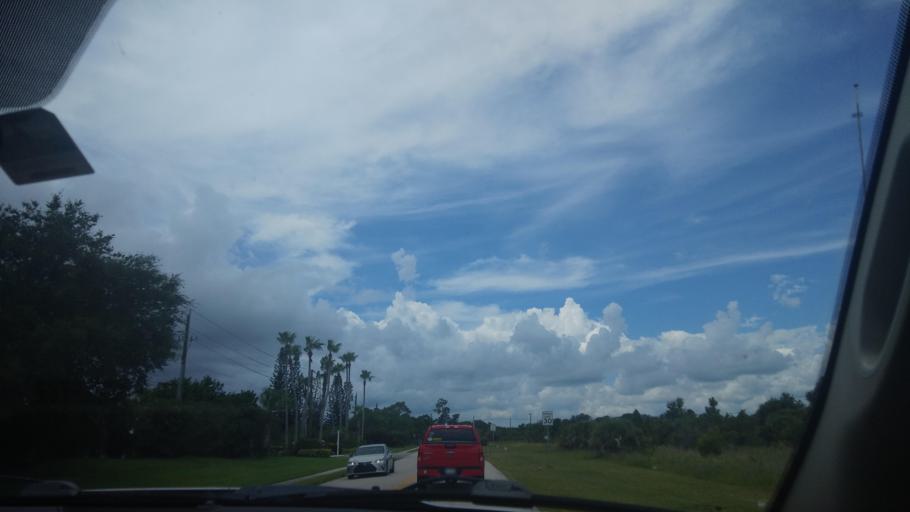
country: US
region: Florida
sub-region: Indian River County
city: Wabasso Beach
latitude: 27.7653
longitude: -80.4504
